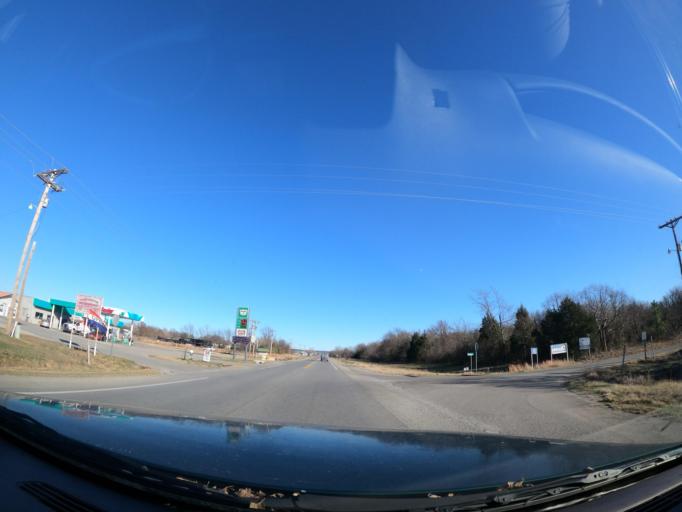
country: US
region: Oklahoma
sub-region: Pittsburg County
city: Longtown
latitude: 35.2392
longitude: -95.5174
